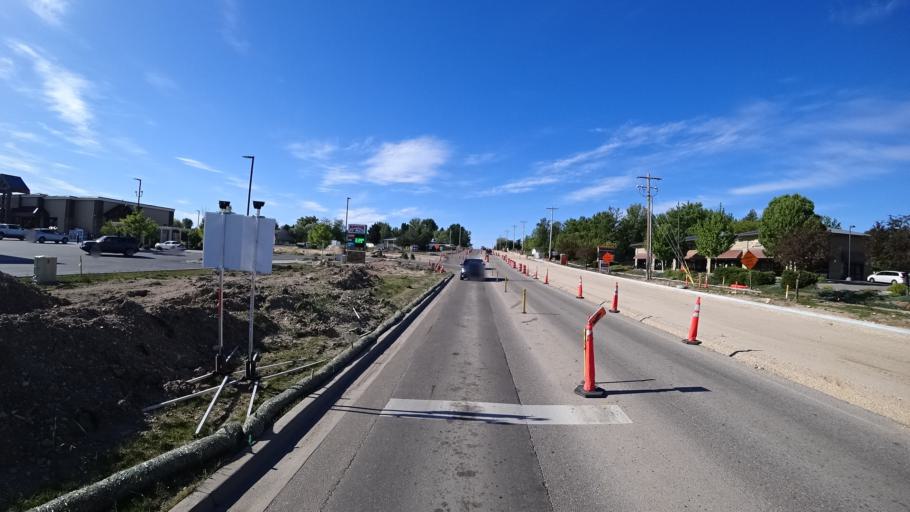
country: US
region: Idaho
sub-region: Ada County
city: Garden City
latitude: 43.5754
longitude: -116.2740
